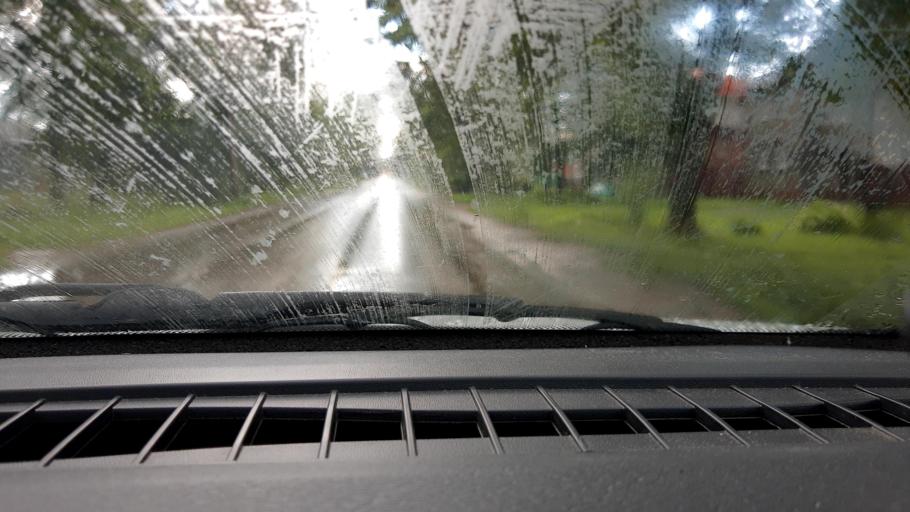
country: RU
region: Nizjnij Novgorod
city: Bogorodsk
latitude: 56.0966
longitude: 43.5089
